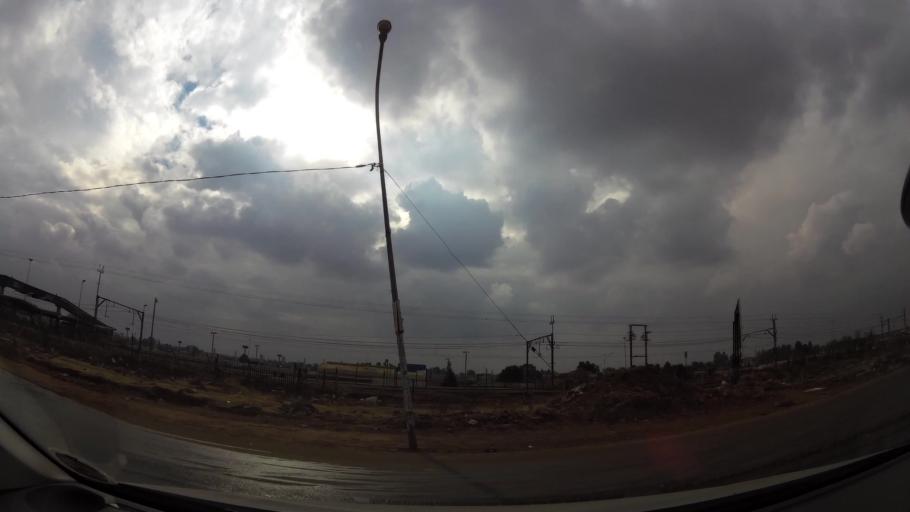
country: ZA
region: Gauteng
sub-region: City of Johannesburg Metropolitan Municipality
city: Soweto
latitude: -26.2622
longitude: 27.8480
